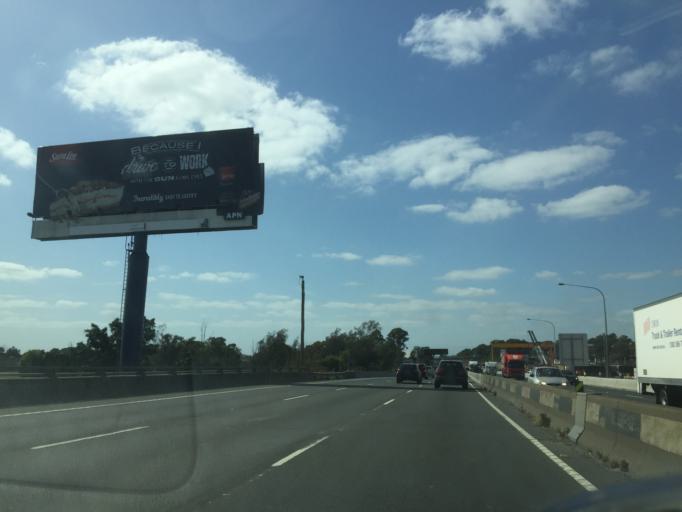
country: AU
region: New South Wales
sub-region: Parramatta
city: Granville
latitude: -33.8356
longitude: 151.0307
